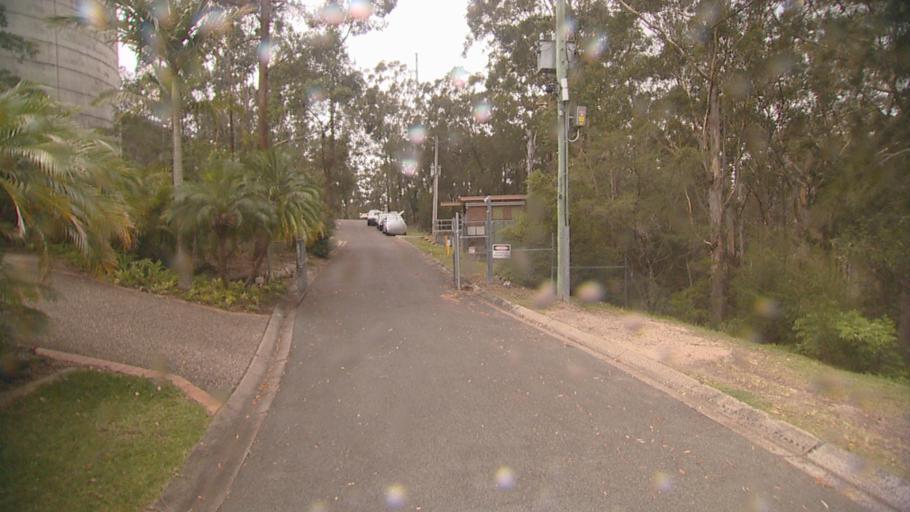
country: AU
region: Queensland
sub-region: Logan
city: Slacks Creek
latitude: -27.6467
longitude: 153.1910
